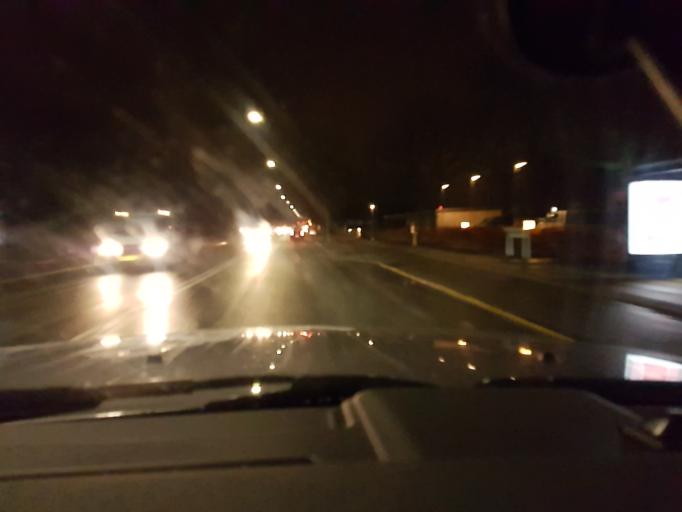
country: DK
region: Capital Region
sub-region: Tarnby Kommune
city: Tarnby
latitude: 55.6491
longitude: 12.5919
